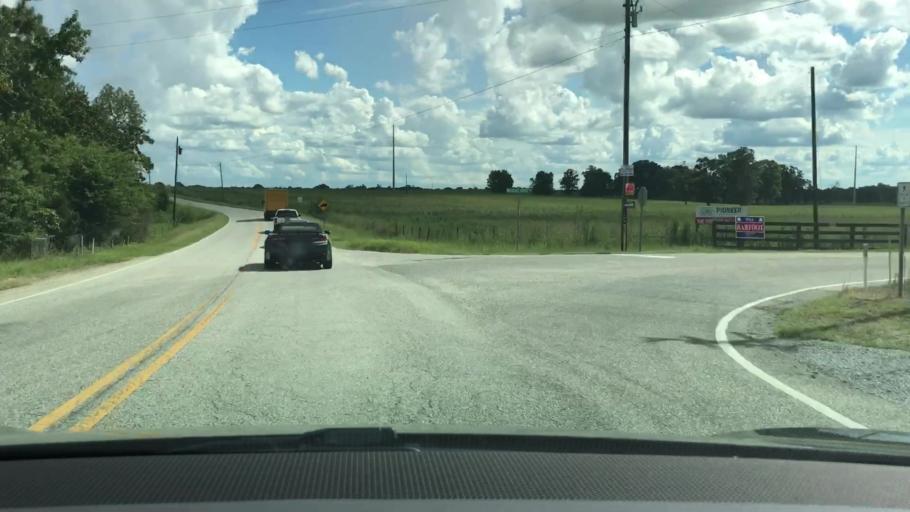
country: US
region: Alabama
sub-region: Montgomery County
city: Pike Road
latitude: 32.2819
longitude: -86.1026
